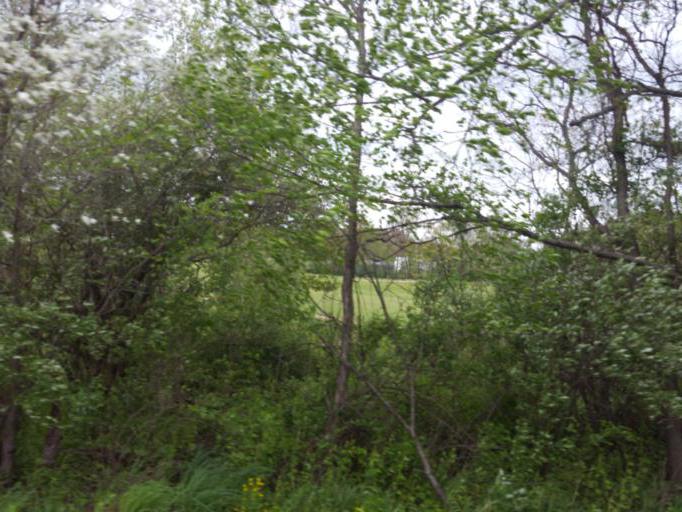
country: US
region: Ohio
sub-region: Ashland County
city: Loudonville
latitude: 40.5593
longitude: -82.3036
